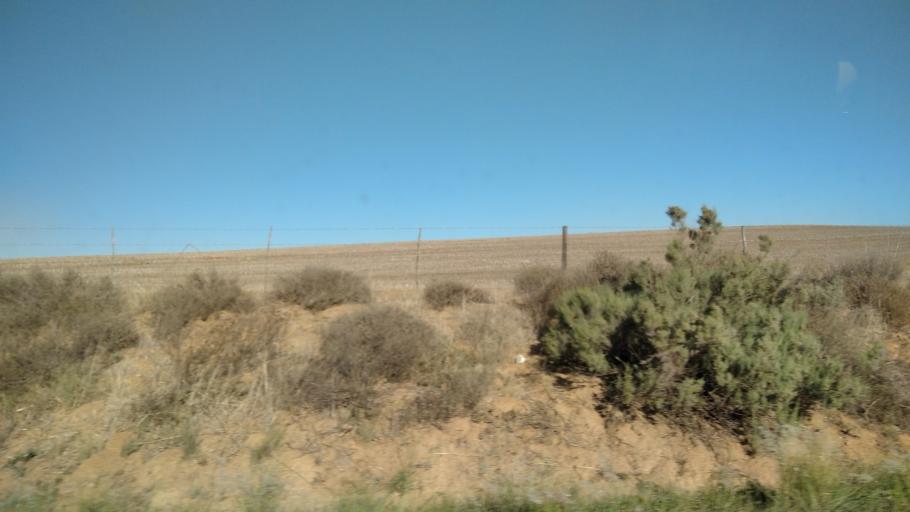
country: ZA
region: Western Cape
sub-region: West Coast District Municipality
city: Malmesbury
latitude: -33.3854
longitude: 18.6704
